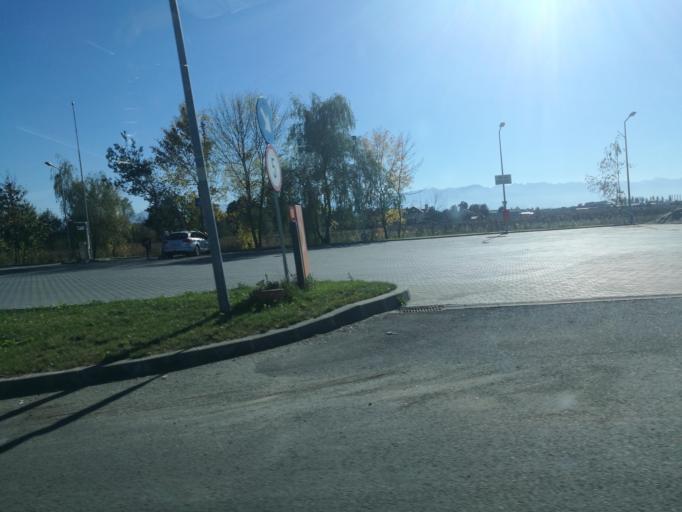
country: RO
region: Brasov
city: Fogarasch
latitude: 45.8370
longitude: 24.9983
